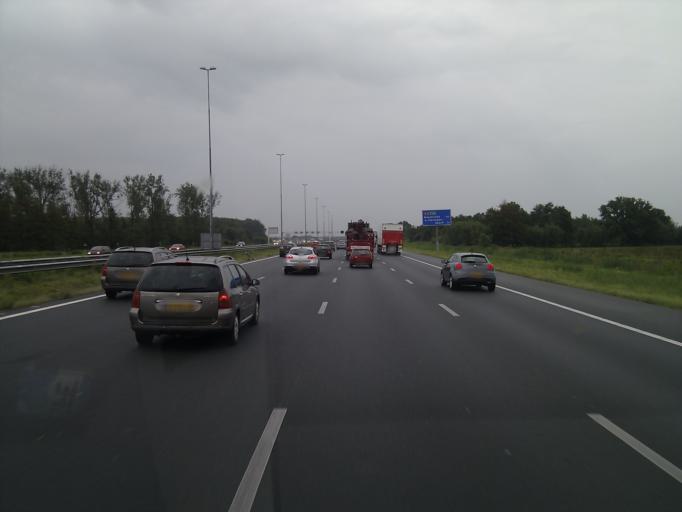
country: NL
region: Utrecht
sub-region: Gemeente Vianen
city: Vianen
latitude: 51.9605
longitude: 5.1186
